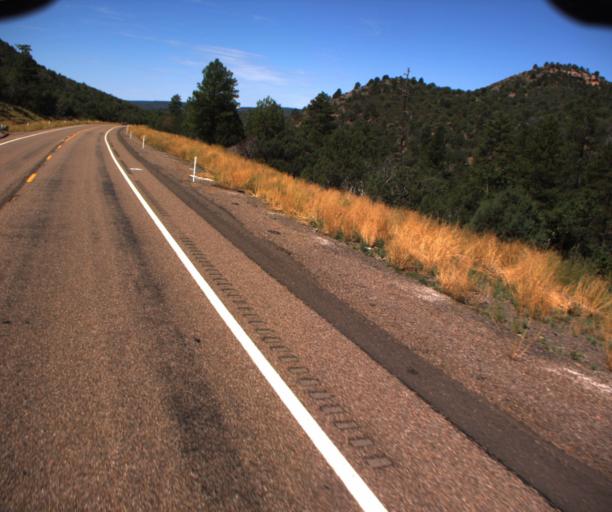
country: US
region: Arizona
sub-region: Navajo County
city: Cibecue
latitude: 33.8960
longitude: -110.3707
